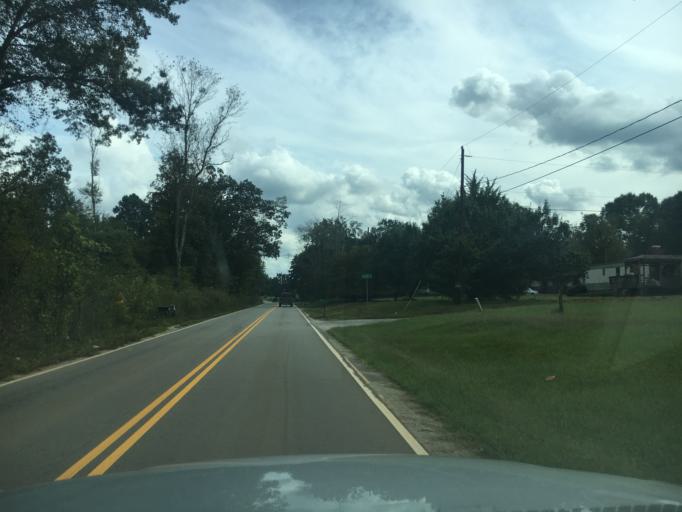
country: US
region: South Carolina
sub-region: Spartanburg County
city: Wellford
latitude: 34.9188
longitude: -82.0610
